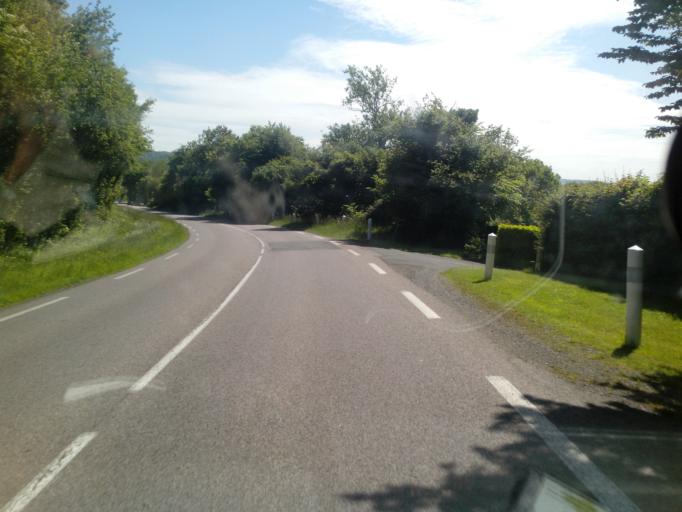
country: FR
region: Lower Normandy
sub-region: Departement du Calvados
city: Saint-Gatien-des-Bois
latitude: 49.3111
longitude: 0.2596
